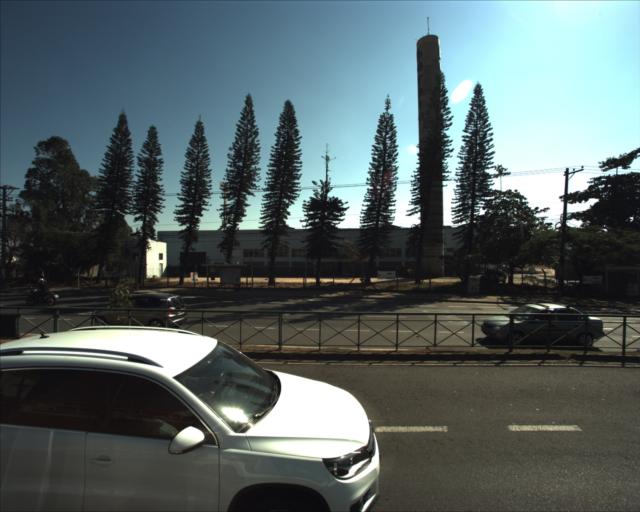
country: BR
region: Sao Paulo
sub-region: Sorocaba
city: Sorocaba
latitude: -23.4898
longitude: -47.4285
